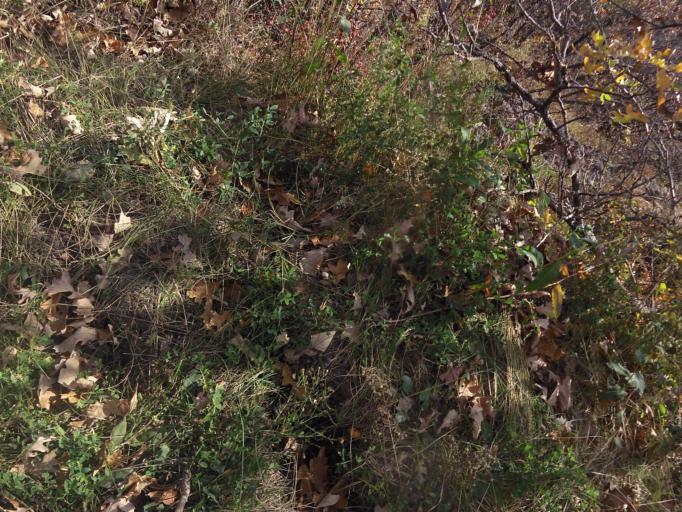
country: CA
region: Manitoba
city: Morden
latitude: 48.9479
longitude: -98.0659
